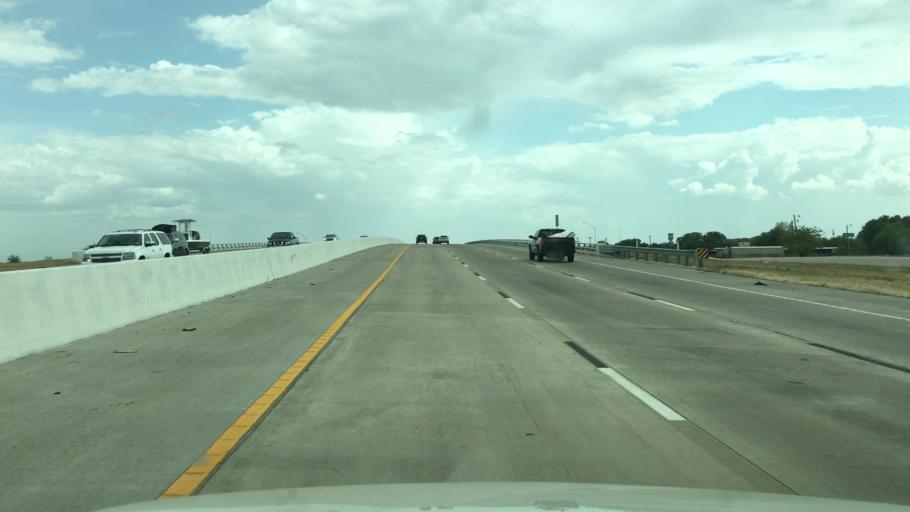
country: US
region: Texas
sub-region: McLennan County
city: Northcrest
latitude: 31.7186
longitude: -97.1026
